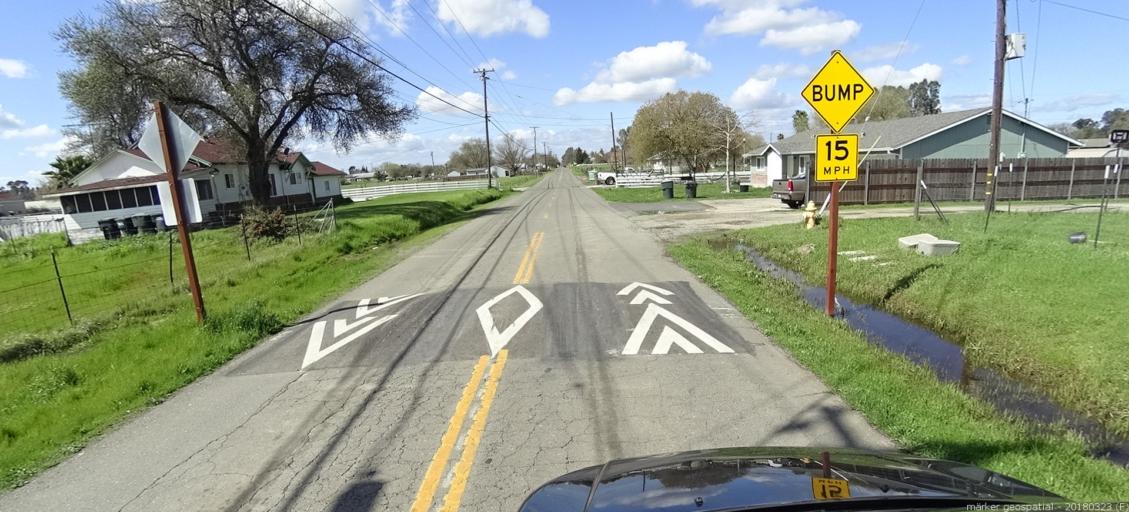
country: US
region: California
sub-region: Sacramento County
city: Rio Linda
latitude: 38.6834
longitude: -121.4127
